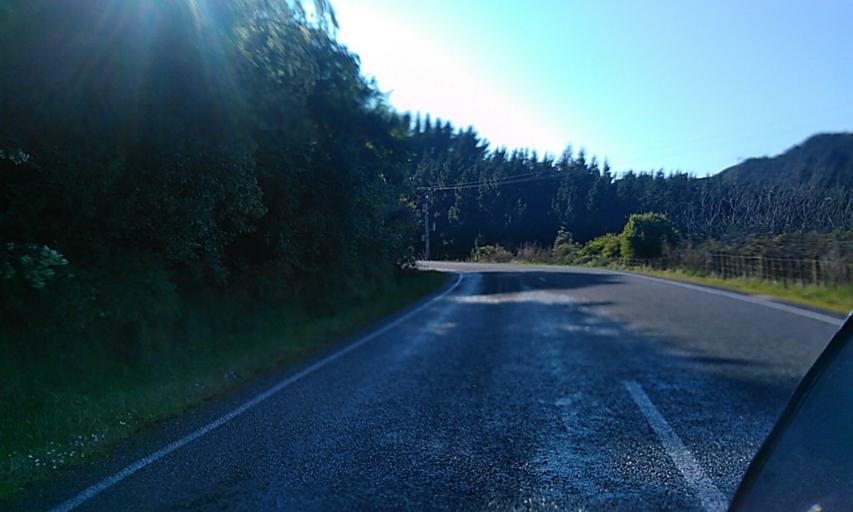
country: NZ
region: Gisborne
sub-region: Gisborne District
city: Gisborne
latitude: -38.5940
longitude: 177.9772
